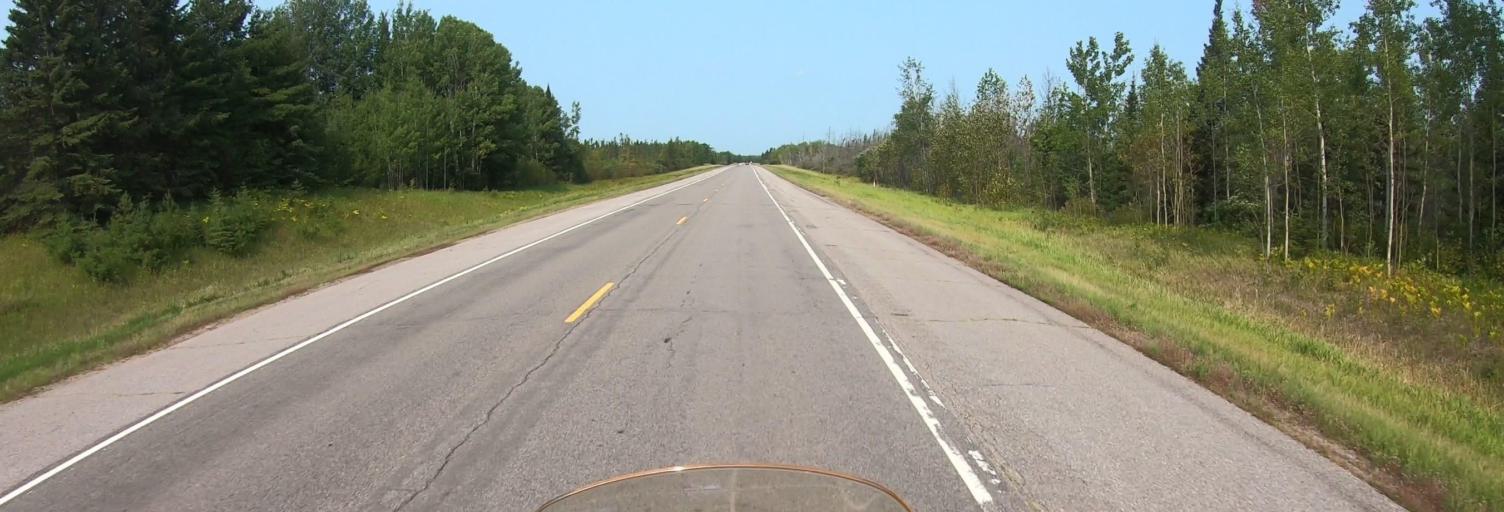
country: US
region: Minnesota
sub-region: Saint Louis County
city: Mountain Iron
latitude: 47.8689
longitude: -92.7426
